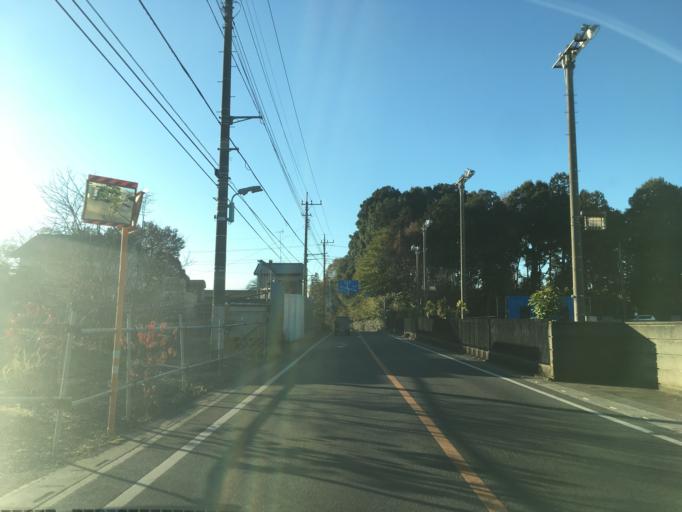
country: JP
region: Saitama
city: Tokorozawa
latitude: 35.7917
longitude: 139.4154
